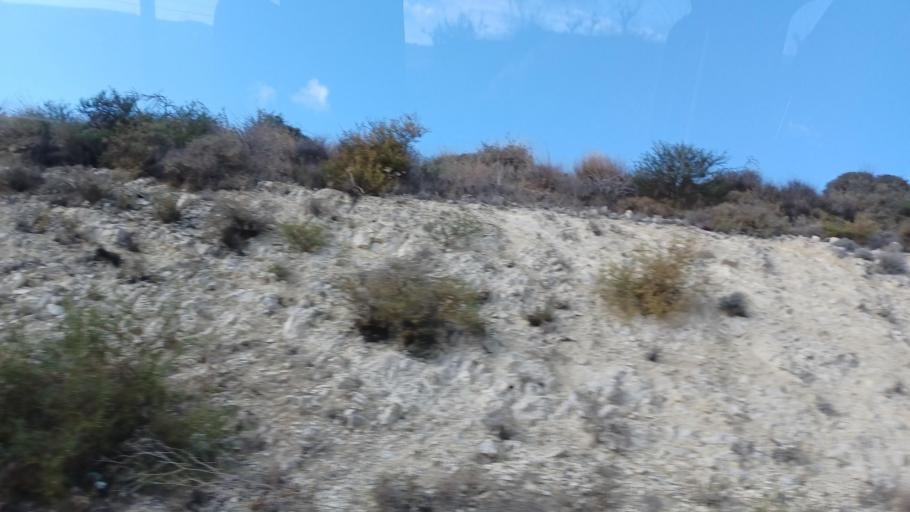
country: CY
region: Limassol
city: Pachna
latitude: 34.8371
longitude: 32.8089
